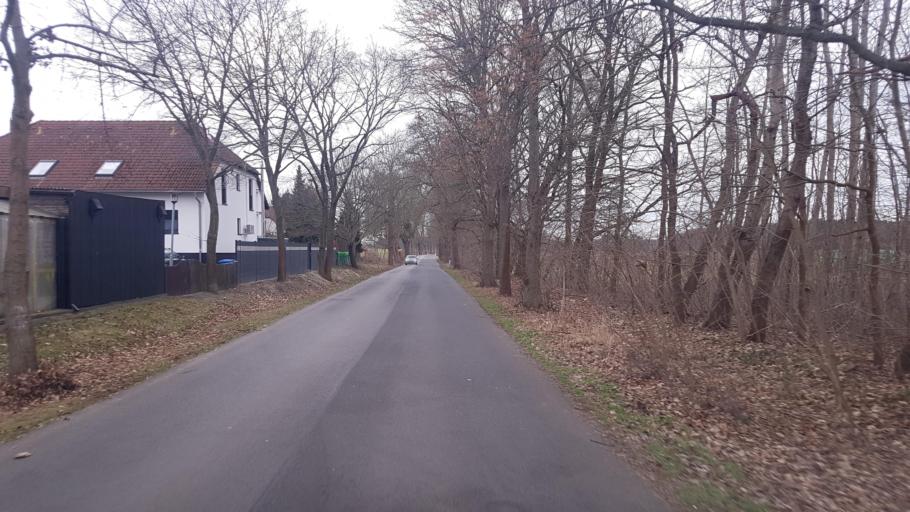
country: DE
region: Brandenburg
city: Halbe
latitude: 52.0874
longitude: 13.7141
